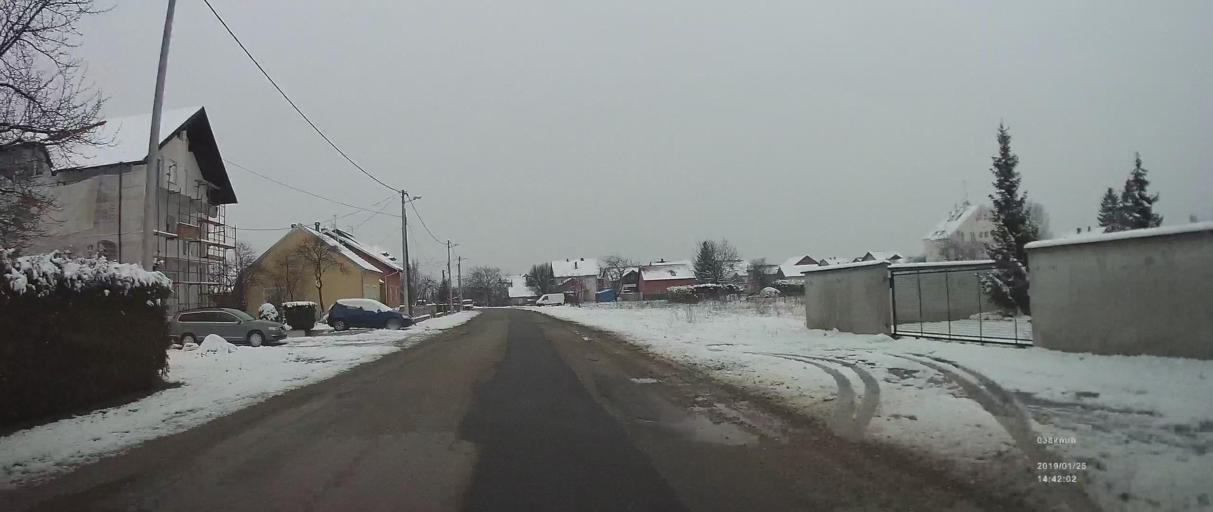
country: HR
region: Zagrebacka
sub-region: Grad Velika Gorica
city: Velika Gorica
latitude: 45.7052
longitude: 16.0729
